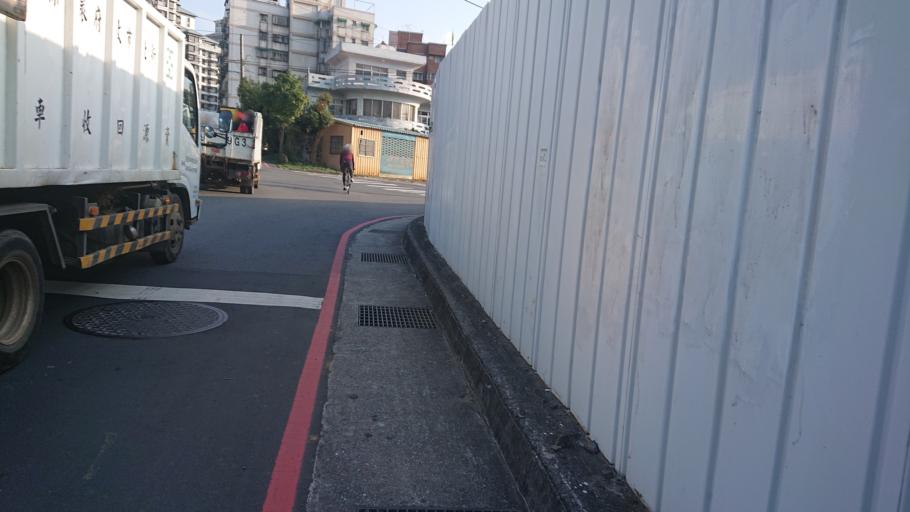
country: TW
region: Taipei
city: Taipei
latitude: 25.1899
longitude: 121.4264
